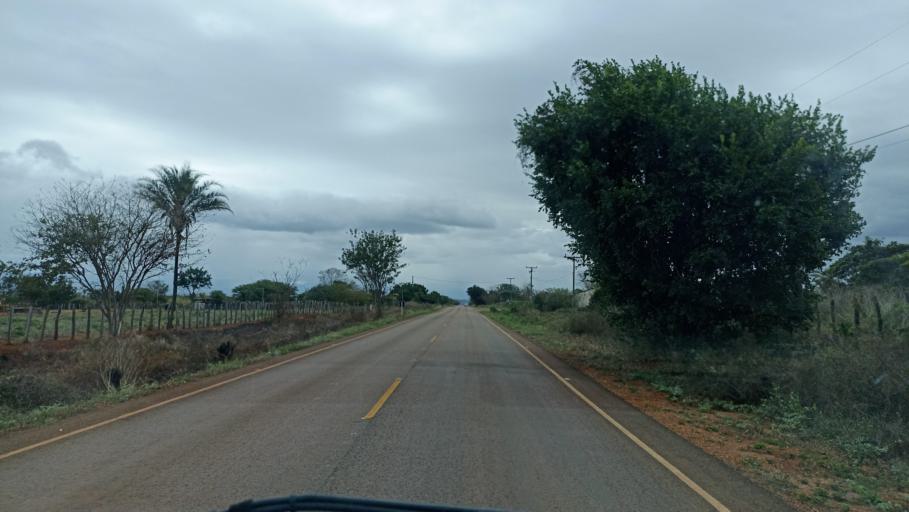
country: BR
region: Bahia
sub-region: Andarai
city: Vera Cruz
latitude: -12.9718
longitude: -41.0257
